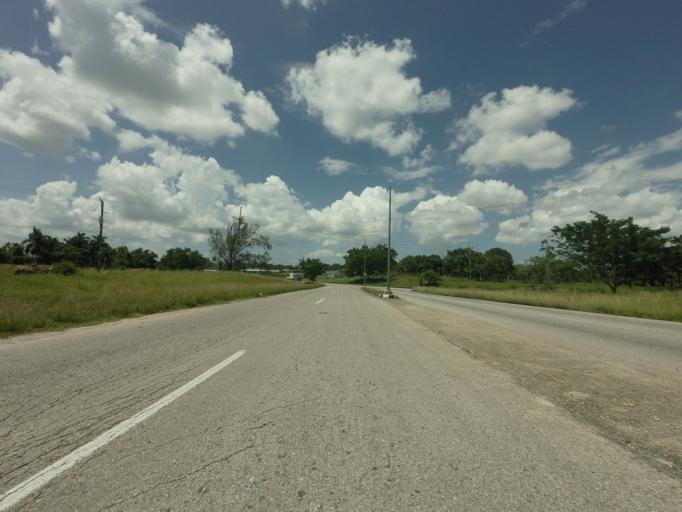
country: CU
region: La Habana
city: Arroyo Naranjo
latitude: 23.0356
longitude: -82.3517
